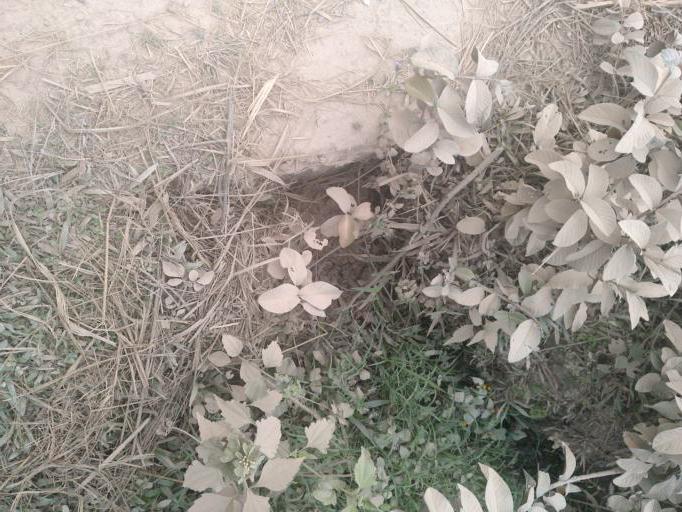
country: LA
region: Xiangkhoang
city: Muang Phonsavan
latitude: 19.3397
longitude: 103.5863
